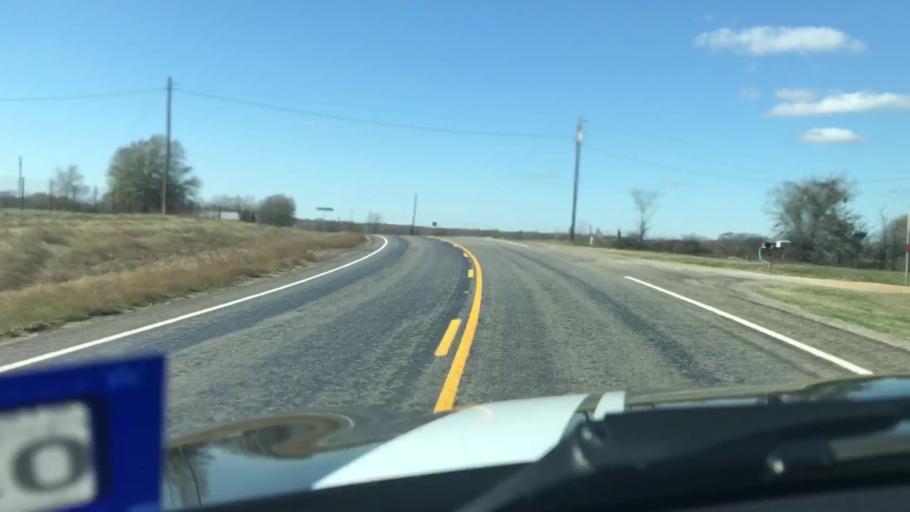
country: US
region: Texas
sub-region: Robertson County
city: Calvert
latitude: 30.8846
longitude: -96.7519
